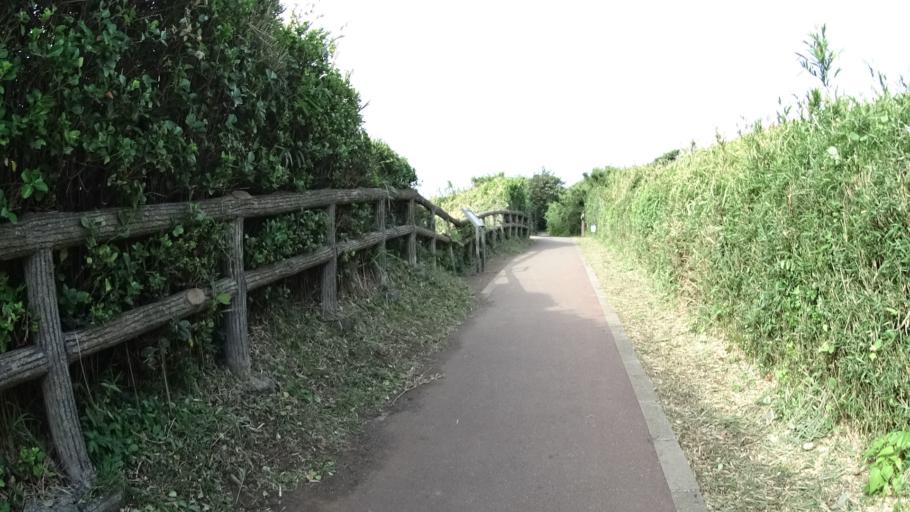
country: JP
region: Kanagawa
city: Miura
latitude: 35.1329
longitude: 139.6211
